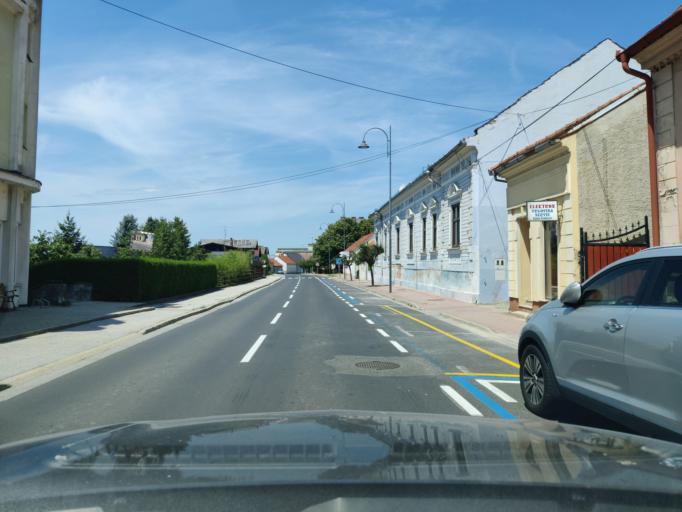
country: SI
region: Lendava-Lendva
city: Lendava
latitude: 46.5683
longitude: 16.4500
